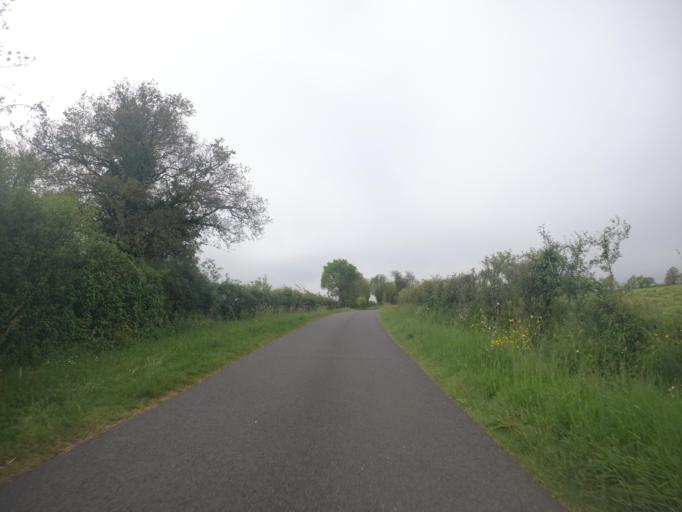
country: FR
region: Poitou-Charentes
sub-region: Departement des Deux-Sevres
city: Chiche
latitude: 46.8698
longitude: -0.3402
